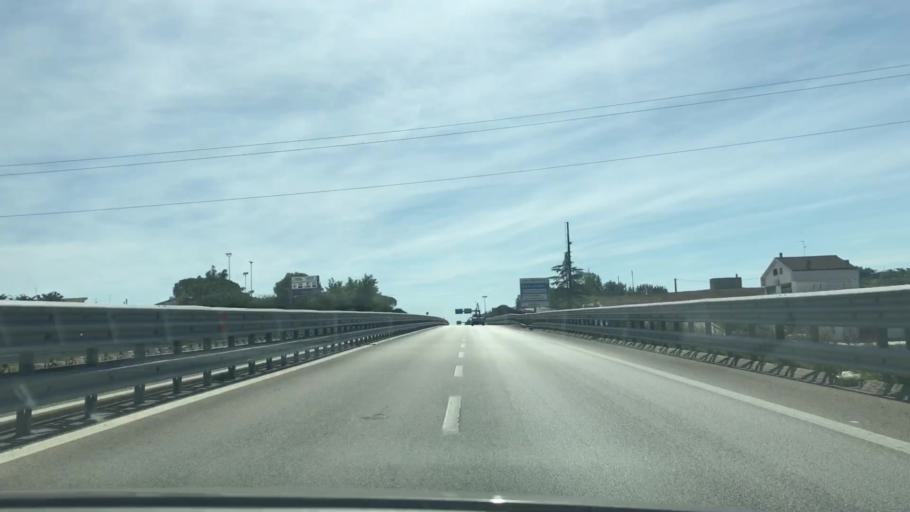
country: IT
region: Basilicate
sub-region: Provincia di Matera
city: Matera
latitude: 40.7062
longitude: 16.5844
